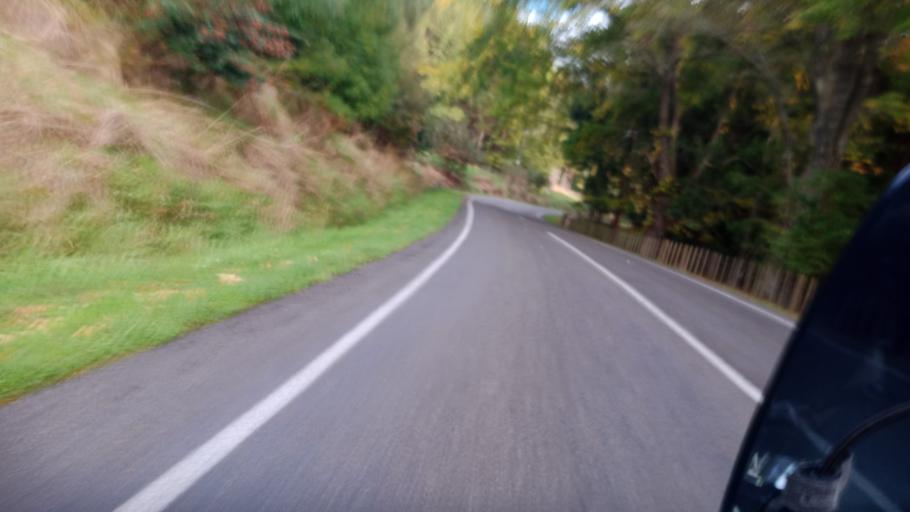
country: NZ
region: Gisborne
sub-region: Gisborne District
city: Gisborne
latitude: -38.5647
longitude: 177.7202
